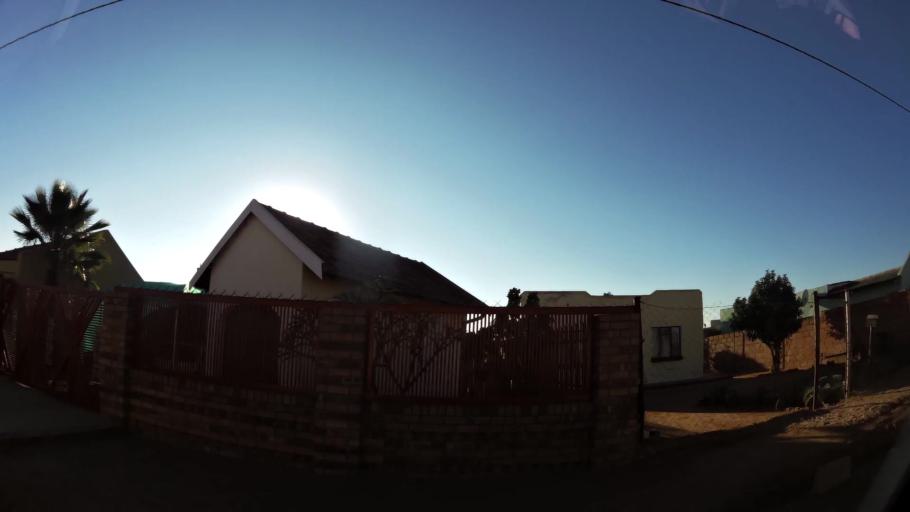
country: ZA
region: Limpopo
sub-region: Capricorn District Municipality
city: Polokwane
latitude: -23.8446
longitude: 29.3582
